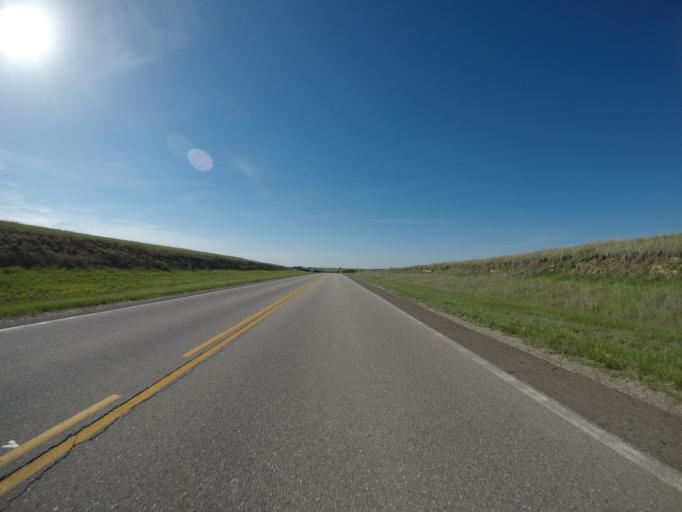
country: US
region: Kansas
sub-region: Clay County
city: Clay Center
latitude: 39.3733
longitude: -96.9523
